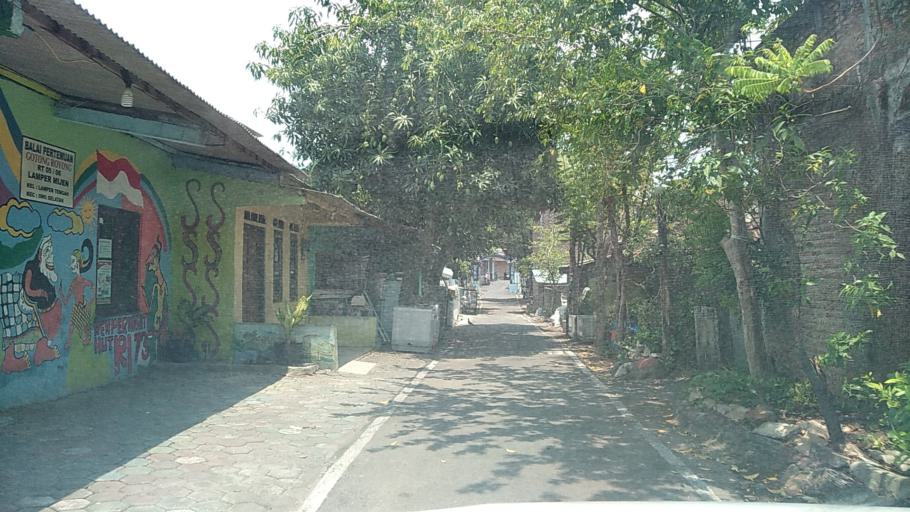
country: ID
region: Central Java
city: Semarang
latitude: -7.0014
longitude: 110.4409
